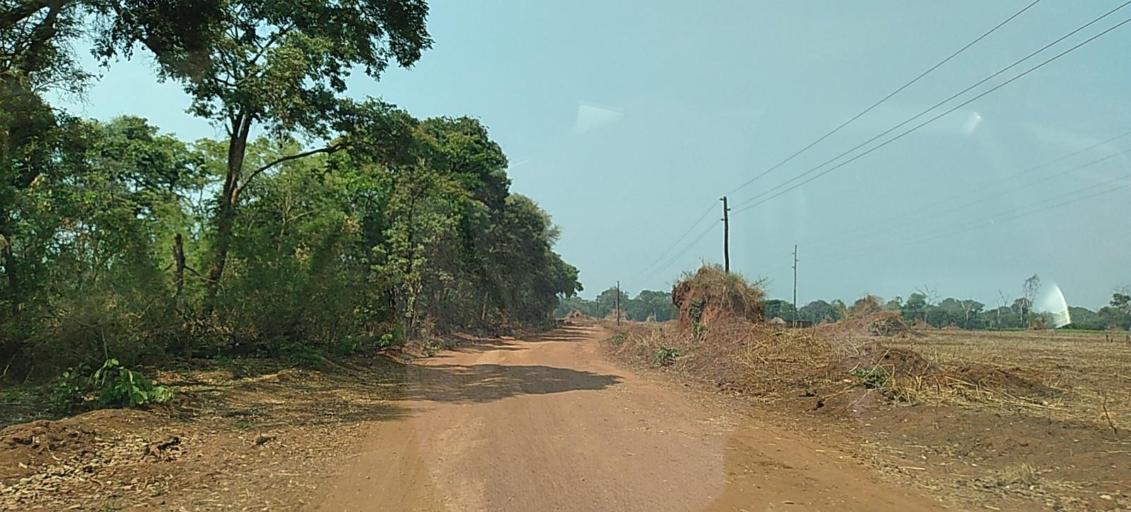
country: ZM
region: Copperbelt
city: Chingola
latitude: -13.0658
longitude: 27.4170
